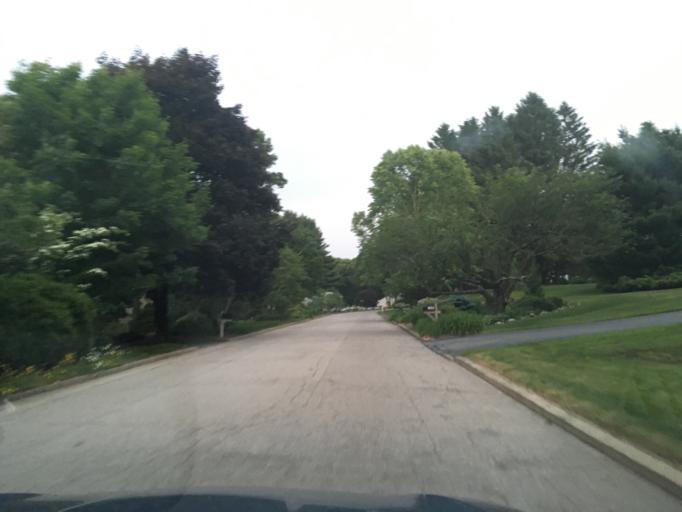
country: US
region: Rhode Island
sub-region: Washington County
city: Exeter
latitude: 41.6331
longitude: -71.5212
